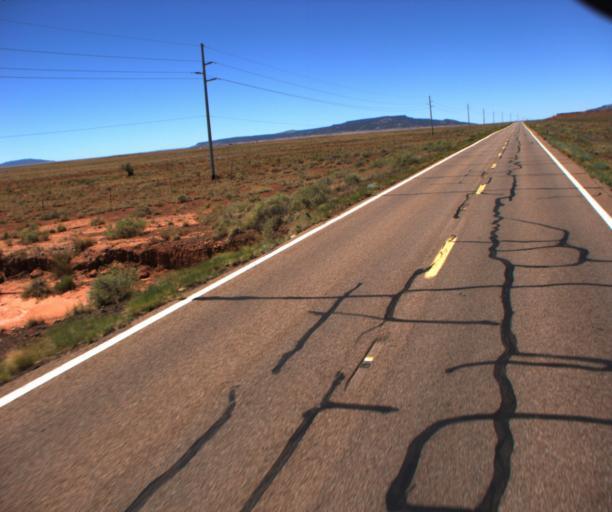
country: US
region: Arizona
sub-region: Coconino County
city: LeChee
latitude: 34.9358
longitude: -110.7885
